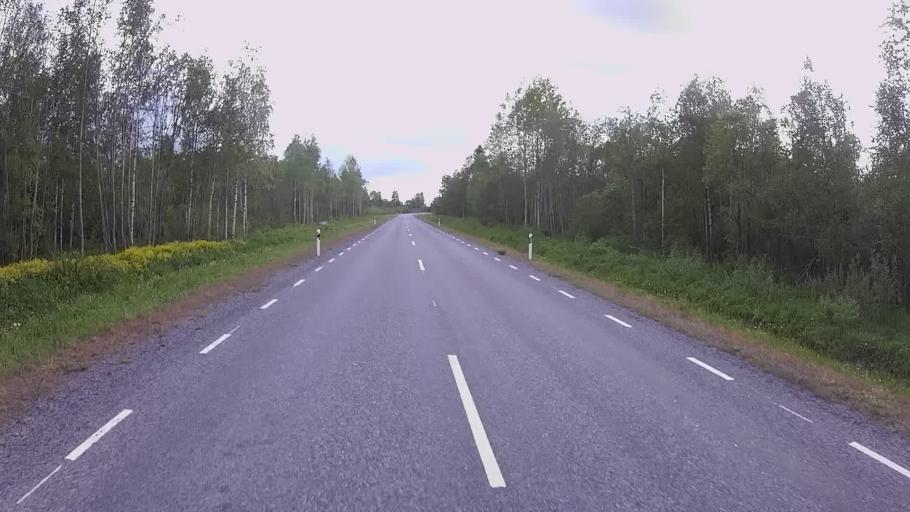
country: EE
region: Jogevamaa
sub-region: Mustvee linn
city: Mustvee
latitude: 59.0113
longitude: 26.9310
